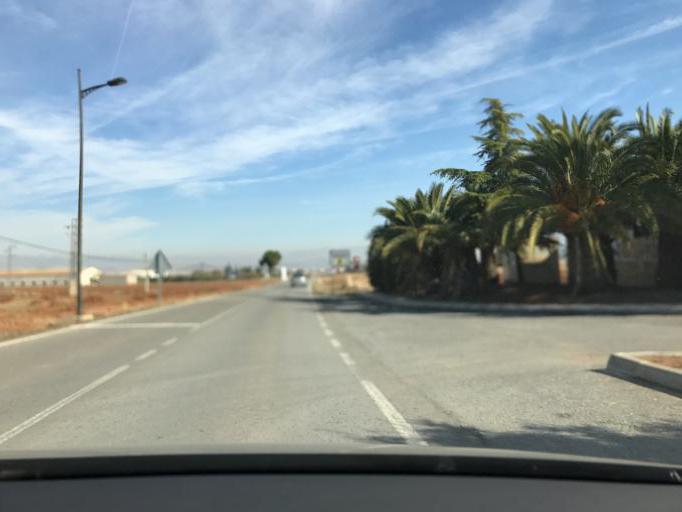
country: ES
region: Andalusia
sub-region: Provincia de Granada
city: Ventas de Huelma
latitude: 37.0699
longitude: -3.8160
